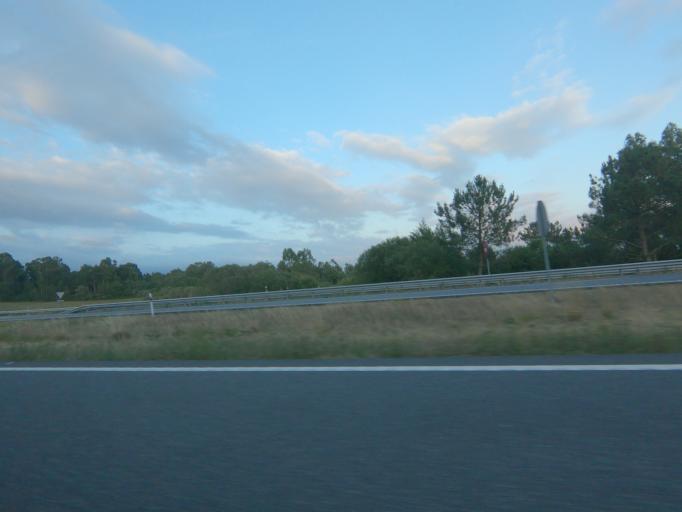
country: ES
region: Galicia
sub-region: Provincia de Ourense
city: Melon
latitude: 42.2165
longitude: -8.2575
